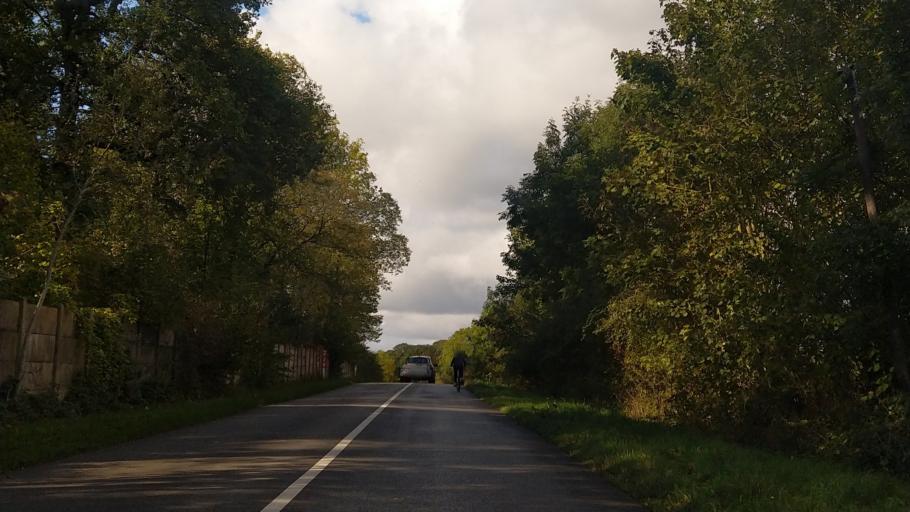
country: FR
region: Ile-de-France
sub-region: Departement du Val-d'Oise
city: Baillet-en-France
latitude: 49.0676
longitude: 2.2903
